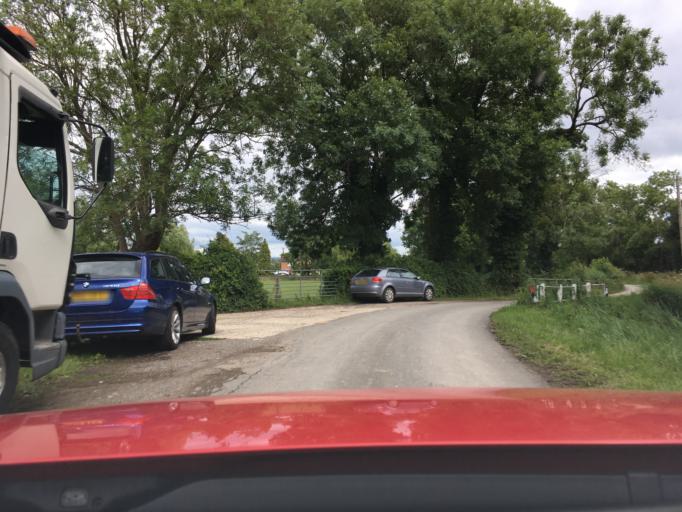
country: GB
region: England
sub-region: Gloucestershire
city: Cinderford
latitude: 51.7994
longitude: -2.4411
